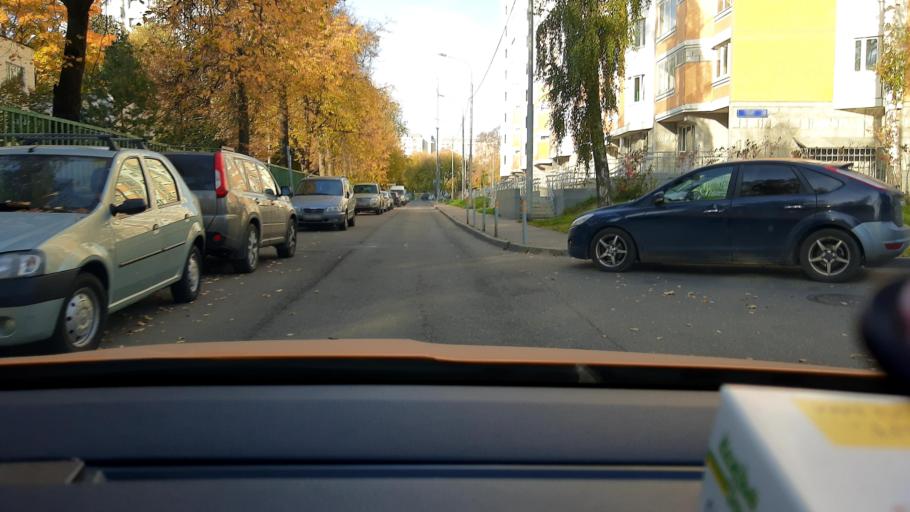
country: RU
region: Moscow
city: Kozeyevo
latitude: 55.8776
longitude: 37.6222
